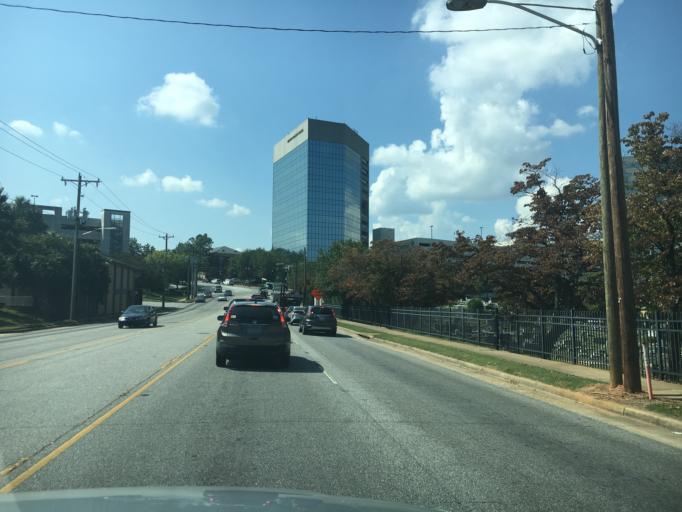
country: US
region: South Carolina
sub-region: Greenville County
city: Greenville
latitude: 34.8543
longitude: -82.3924
